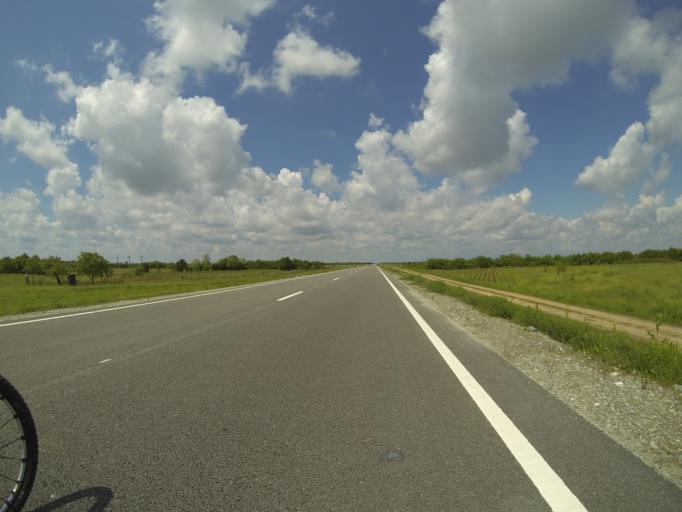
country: RO
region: Dolj
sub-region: Comuna Carcea
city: Carcea
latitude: 44.2770
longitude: 23.9093
